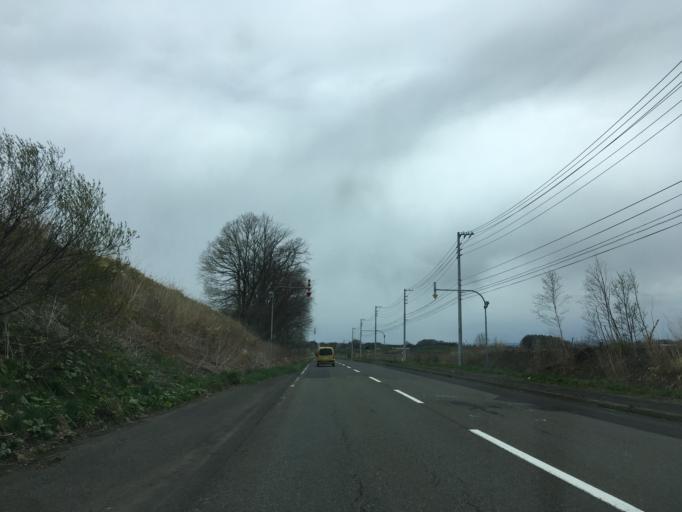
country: JP
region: Hokkaido
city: Chitose
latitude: 42.9019
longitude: 141.8132
